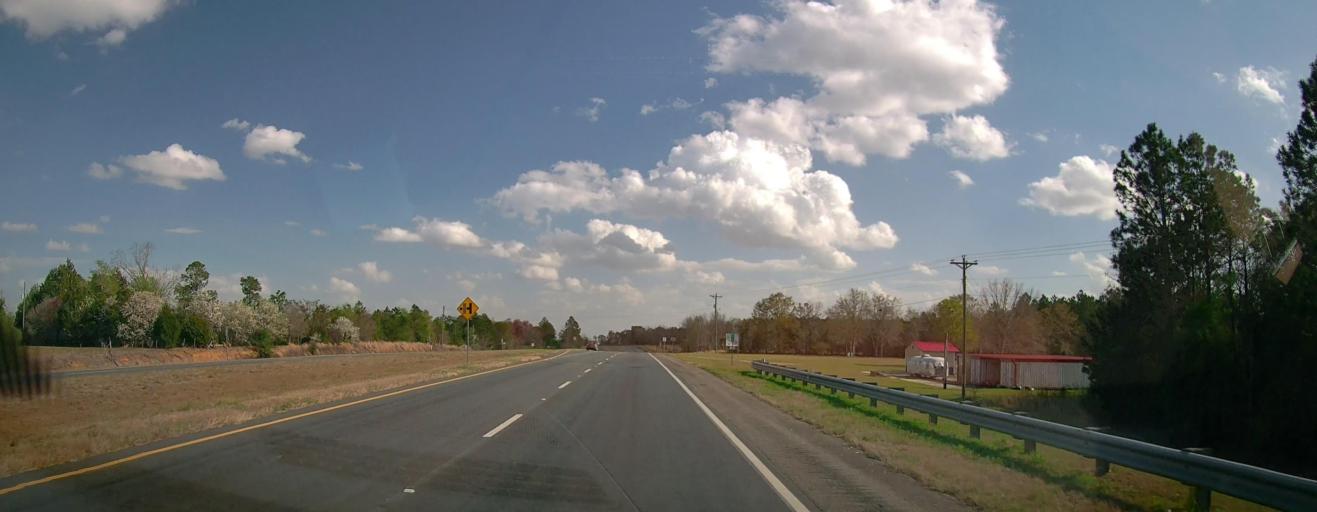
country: US
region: Georgia
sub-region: Dodge County
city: Eastman
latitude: 32.1273
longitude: -83.1204
